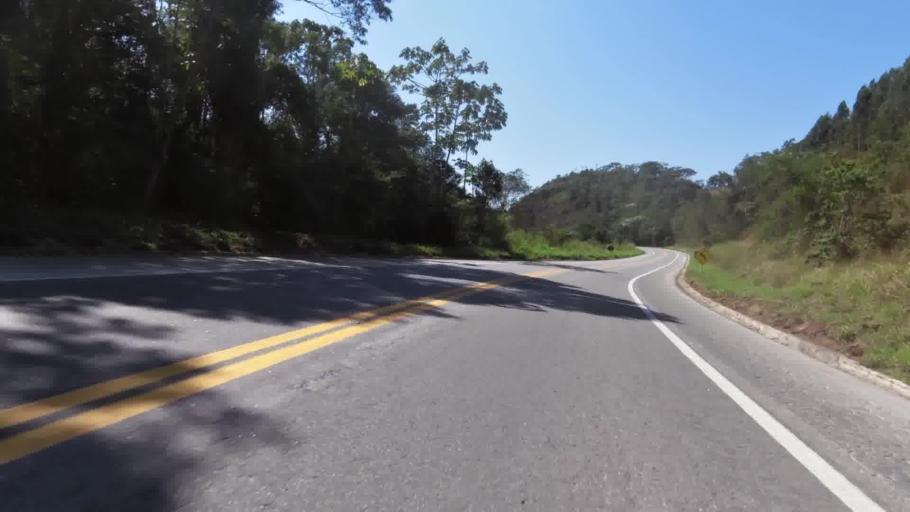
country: BR
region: Espirito Santo
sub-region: Marechal Floriano
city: Marechal Floriano
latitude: -20.4140
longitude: -40.8402
